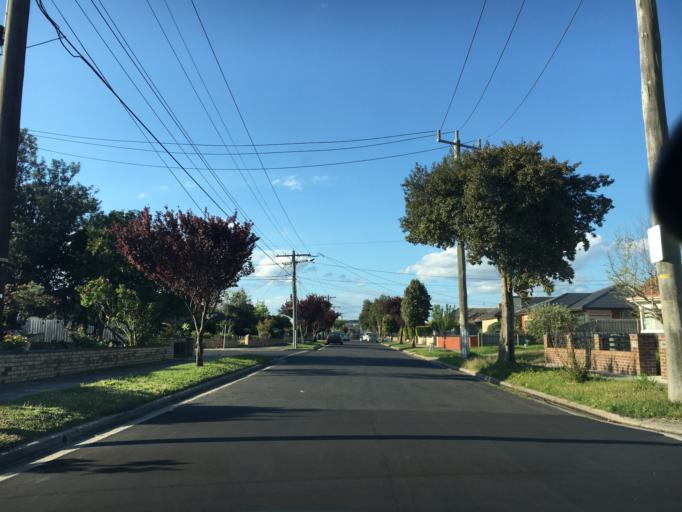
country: AU
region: Victoria
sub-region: Kingston
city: Clayton South
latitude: -37.9345
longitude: 145.1225
